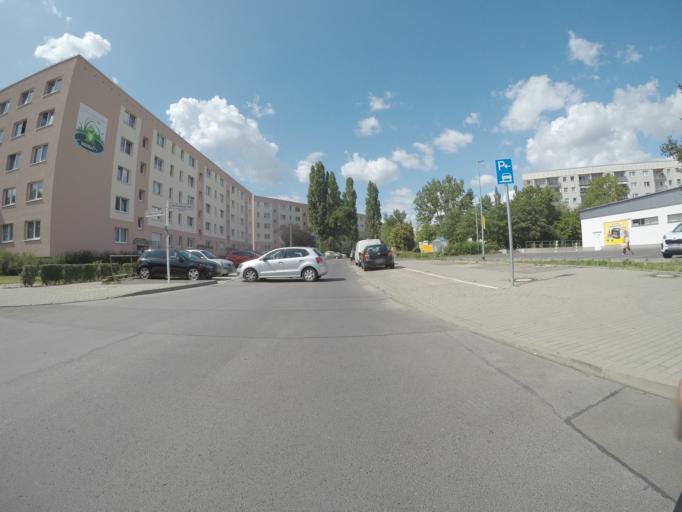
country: DE
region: Berlin
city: Kaulsdorf
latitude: 52.5155
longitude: 13.5831
